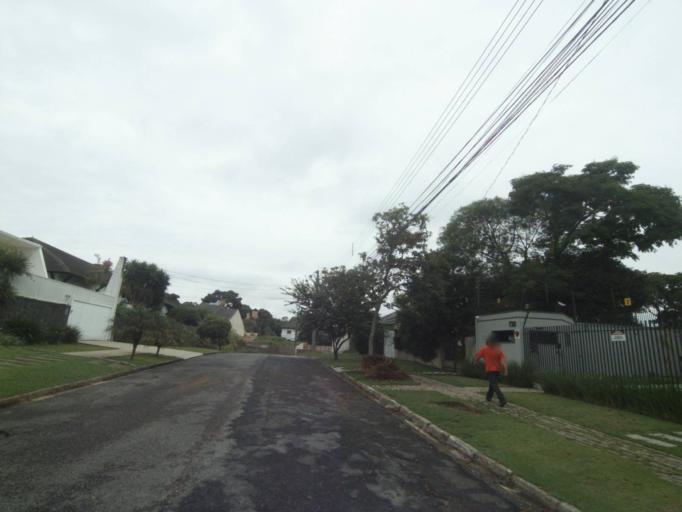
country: BR
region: Parana
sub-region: Curitiba
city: Curitiba
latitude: -25.4076
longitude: -49.2891
